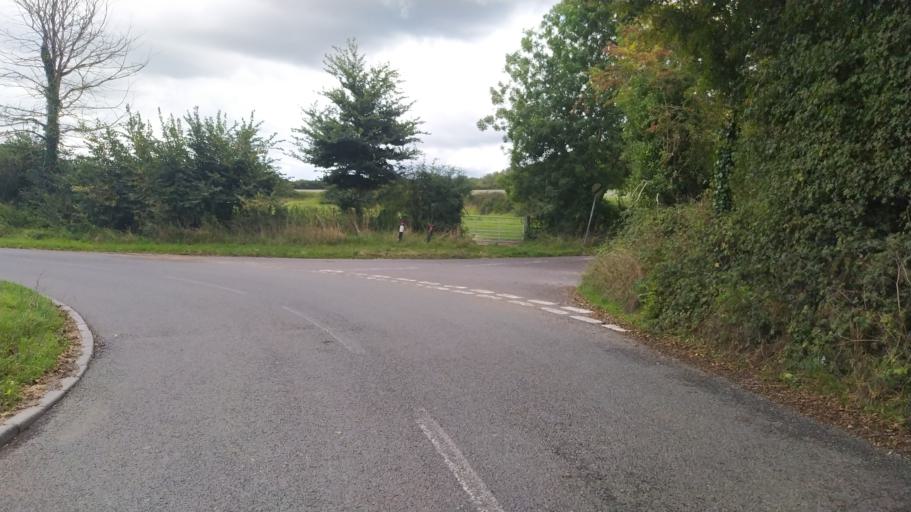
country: GB
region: England
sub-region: Dorset
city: Verwood
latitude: 50.9166
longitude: -1.9166
